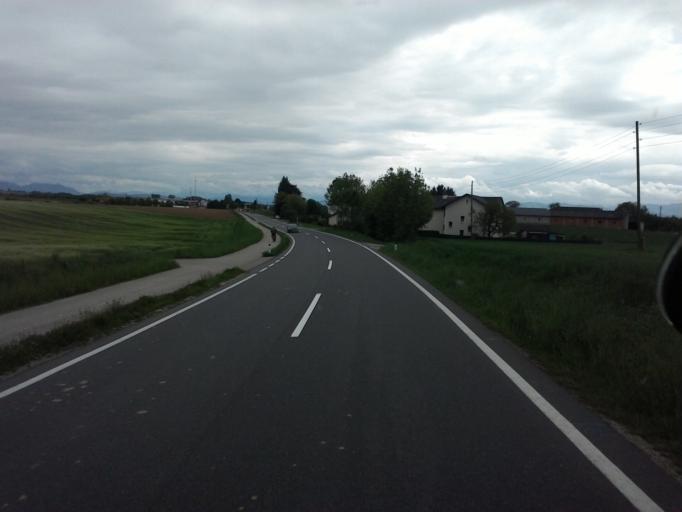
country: AT
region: Upper Austria
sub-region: Wels-Land
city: Sattledt
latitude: 48.0589
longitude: 14.0521
